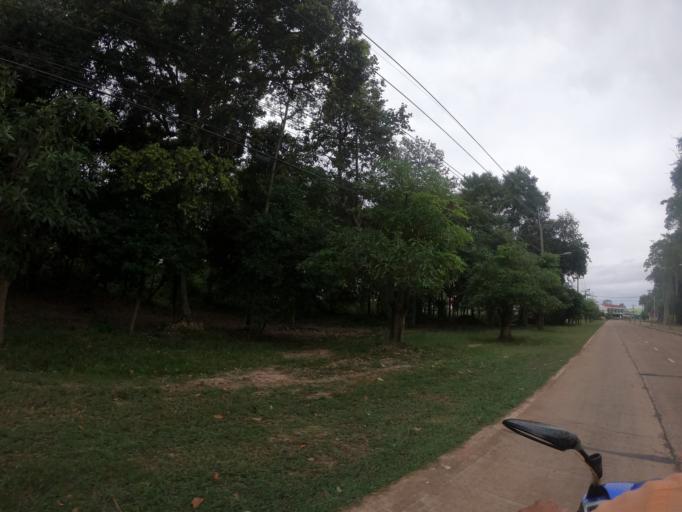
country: TH
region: Roi Et
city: Chiang Khwan
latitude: 16.1459
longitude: 103.8707
